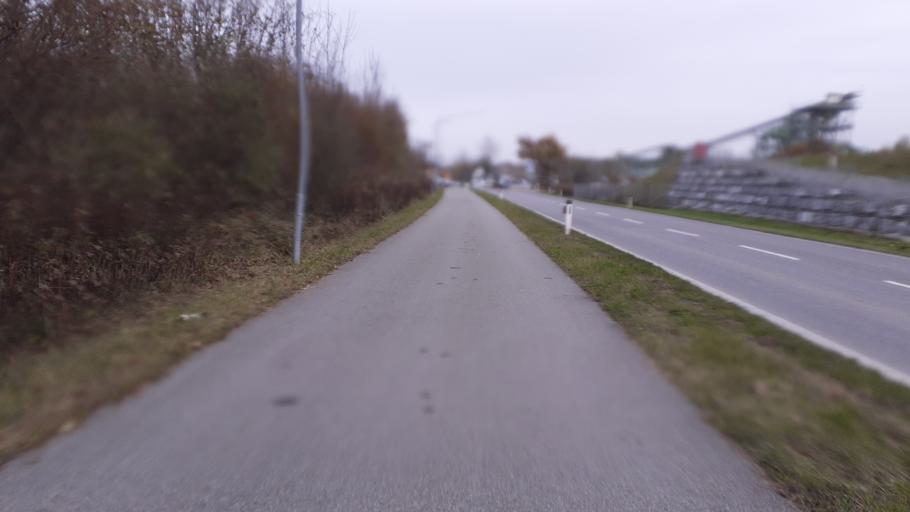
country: AT
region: Vorarlberg
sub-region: Politischer Bezirk Feldkirch
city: Nofels
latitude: 47.2748
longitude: 9.5907
